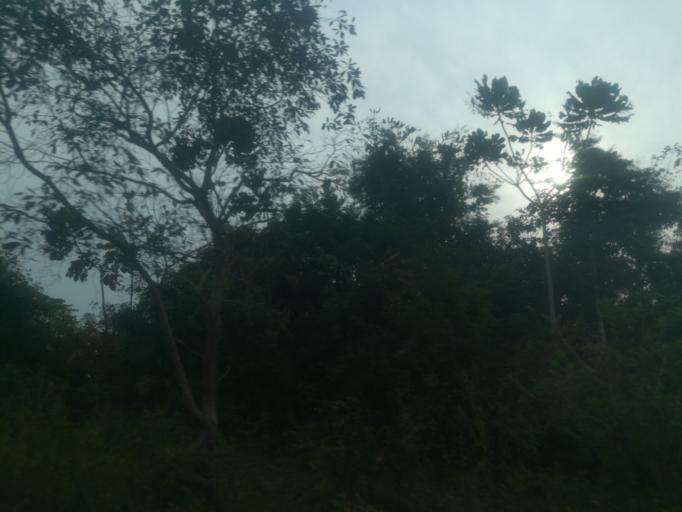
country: NG
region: Ogun
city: Ayetoro
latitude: 7.2739
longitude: 3.0996
